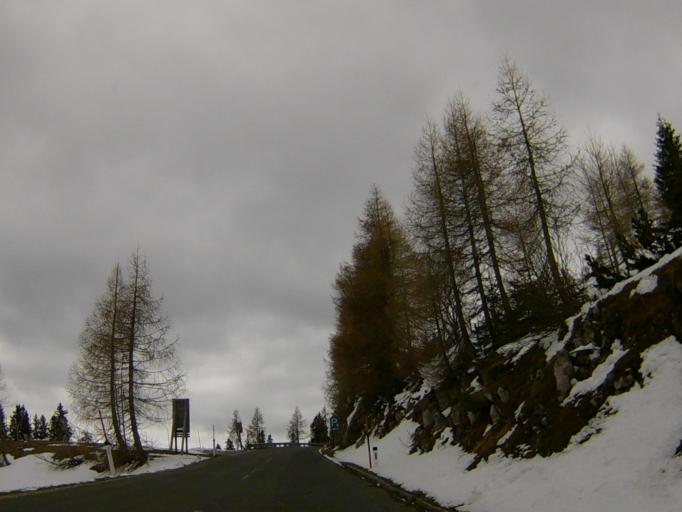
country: AT
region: Carinthia
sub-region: Politischer Bezirk Villach Land
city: Arnoldstein
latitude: 46.5943
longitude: 13.7130
